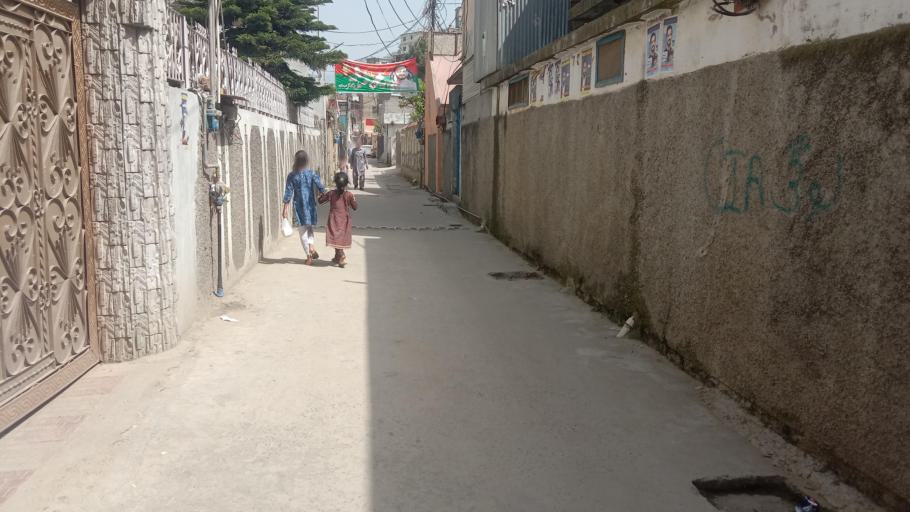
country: PK
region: Khyber Pakhtunkhwa
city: Abbottabad
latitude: 34.1475
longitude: 73.2239
